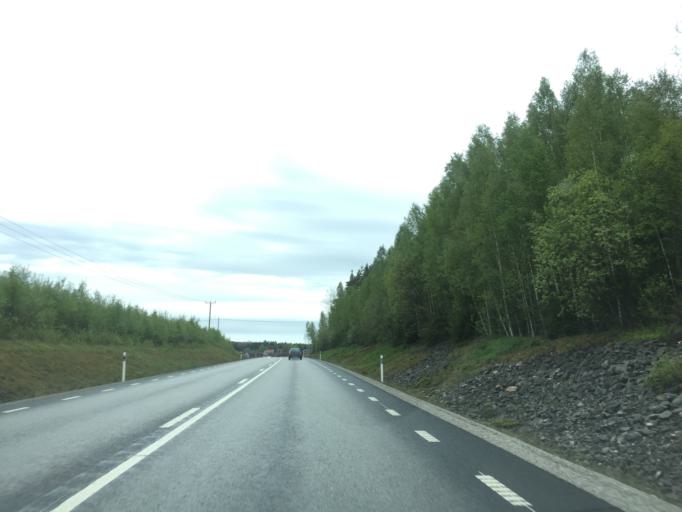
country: SE
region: OErebro
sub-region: Lindesbergs Kommun
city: Lindesberg
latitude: 59.5801
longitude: 15.2016
